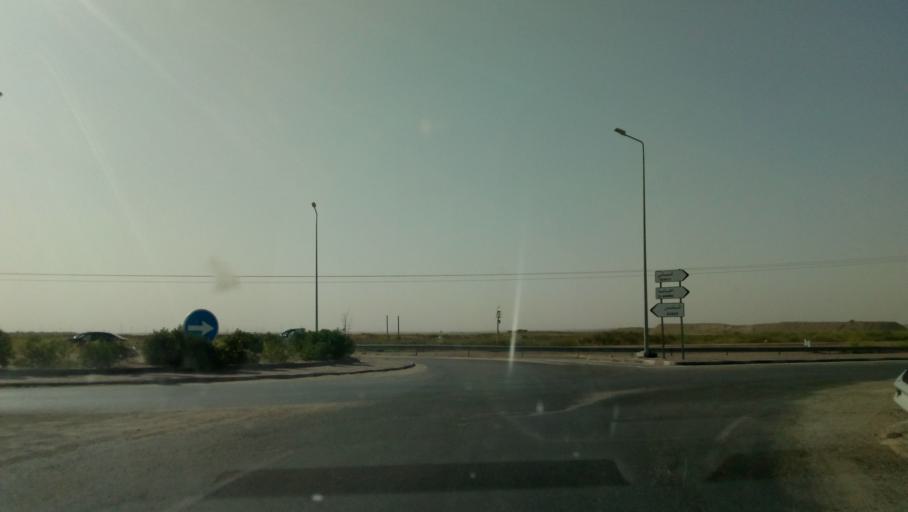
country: TN
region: Qabis
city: Gabes
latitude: 33.8818
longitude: 10.0058
